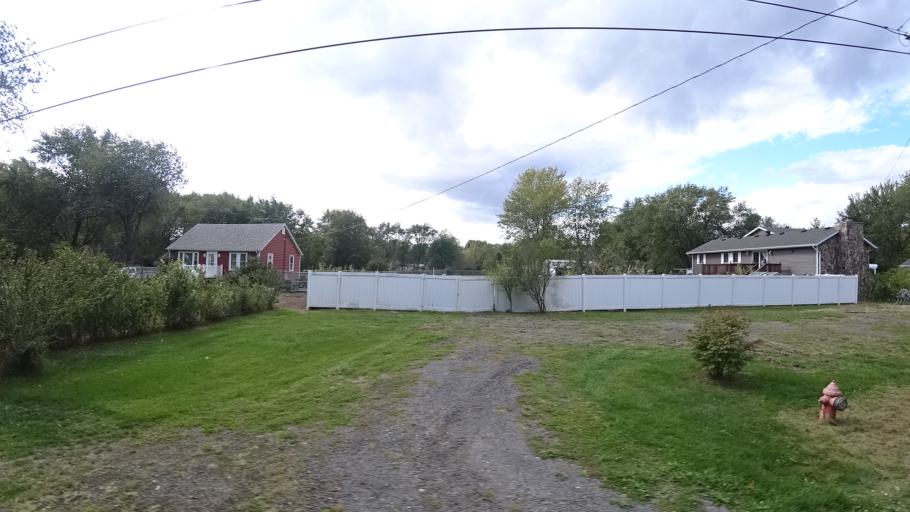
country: US
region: Indiana
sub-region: Porter County
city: Burns Harbor
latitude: 41.6119
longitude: -87.1158
